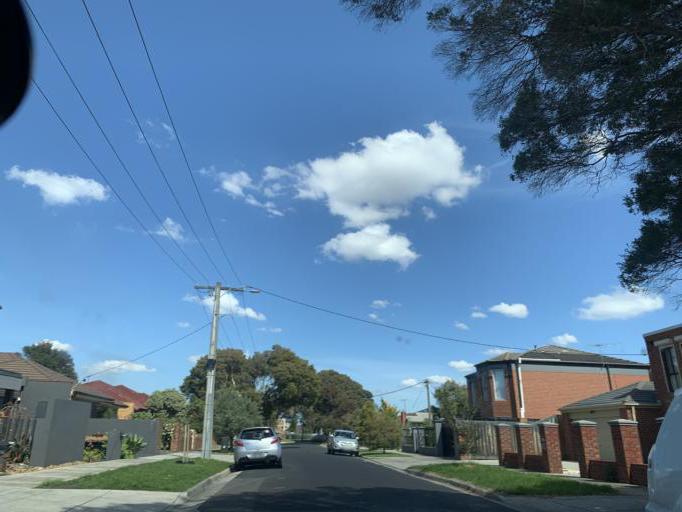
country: AU
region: Victoria
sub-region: Moreland
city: Pascoe Vale
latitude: -37.7326
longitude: 144.9398
